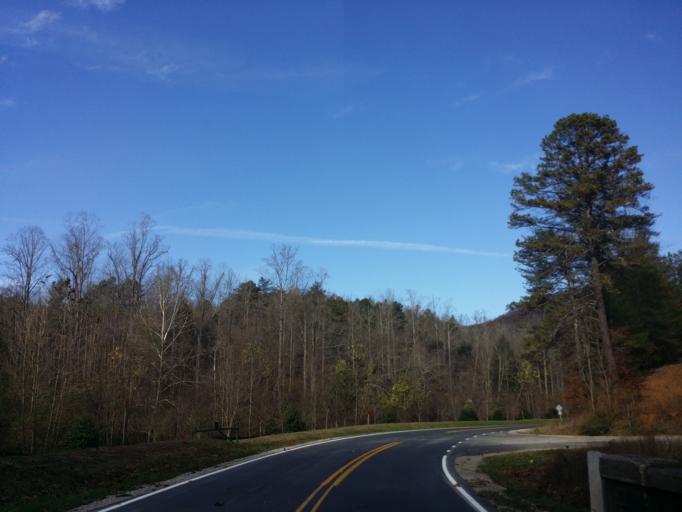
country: US
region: North Carolina
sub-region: McDowell County
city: Marion
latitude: 35.7282
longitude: -82.0923
